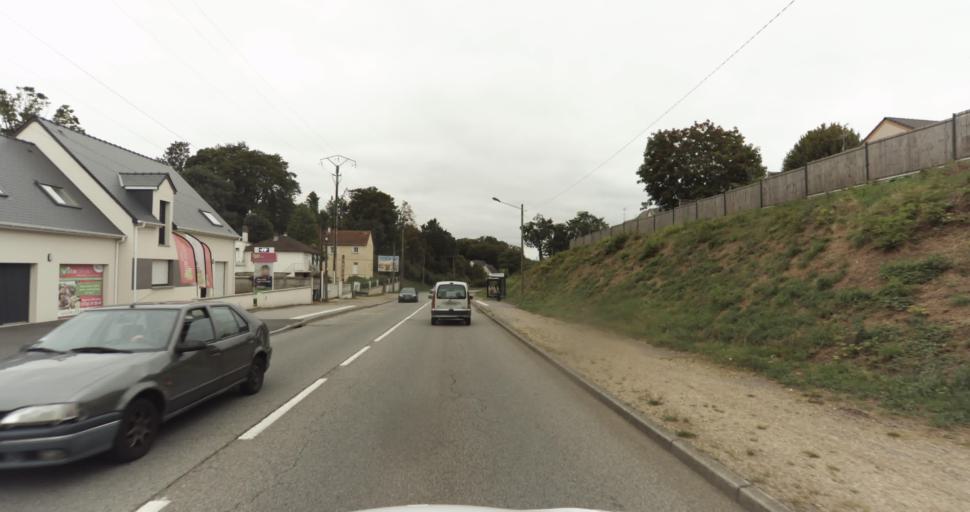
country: FR
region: Haute-Normandie
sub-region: Departement de l'Eure
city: Evreux
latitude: 49.0244
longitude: 1.1682
